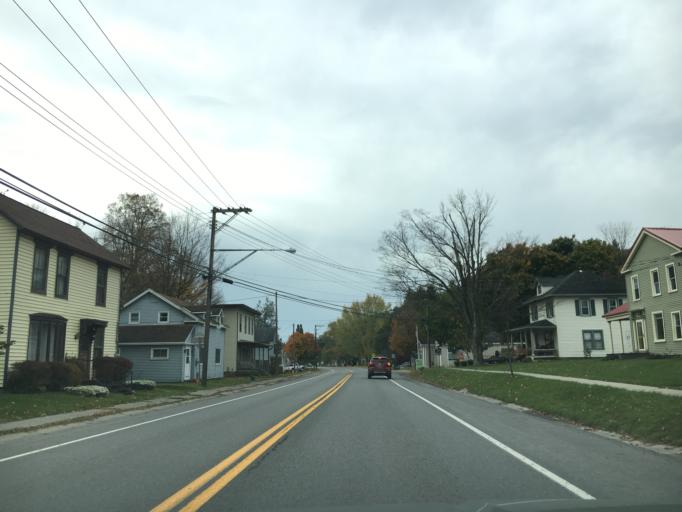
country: US
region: New York
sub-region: Otsego County
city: Cooperstown
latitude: 42.5896
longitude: -74.9461
